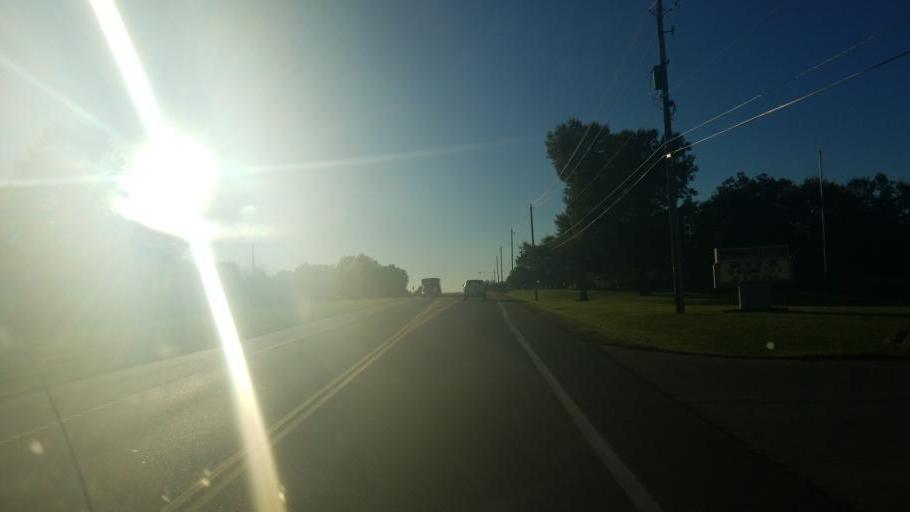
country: US
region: Ohio
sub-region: Mahoning County
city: Sebring
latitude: 40.9015
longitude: -81.0100
